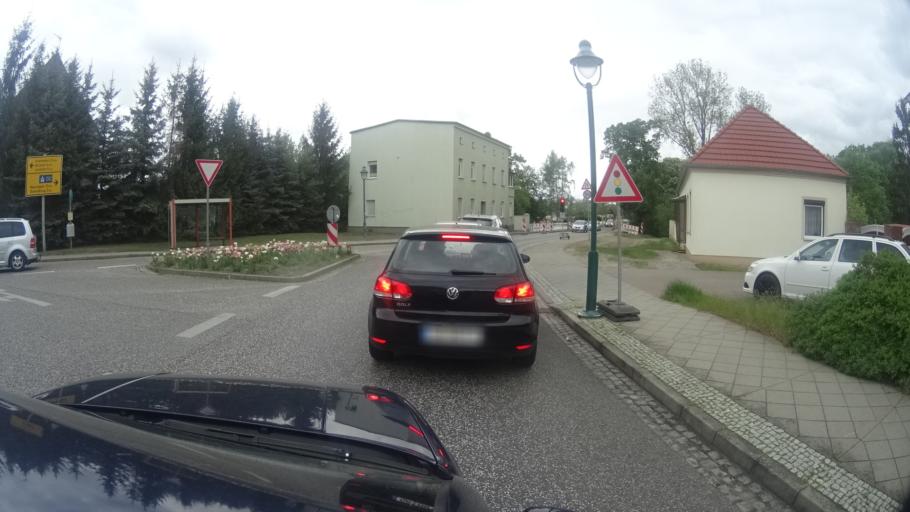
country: DE
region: Brandenburg
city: Fehrbellin
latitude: 52.8152
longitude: 12.7650
